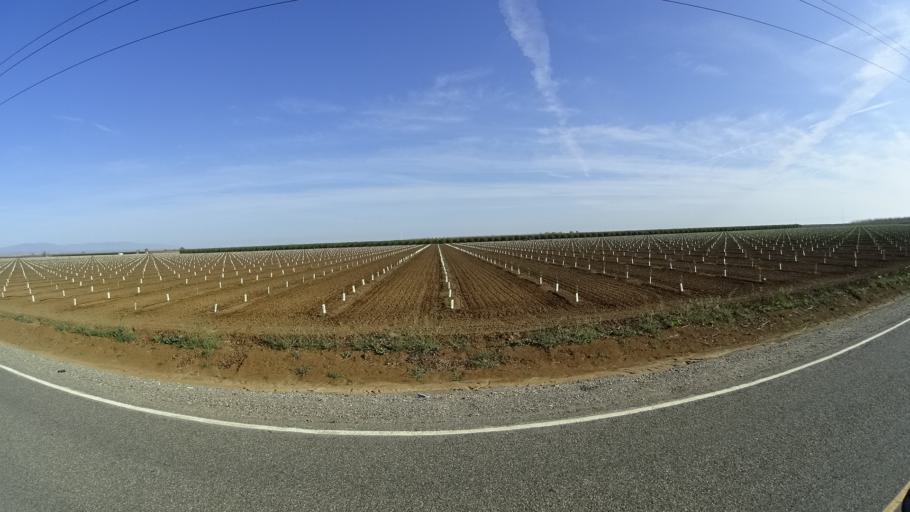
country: US
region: California
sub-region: Glenn County
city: Willows
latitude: 39.5387
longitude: -122.2374
